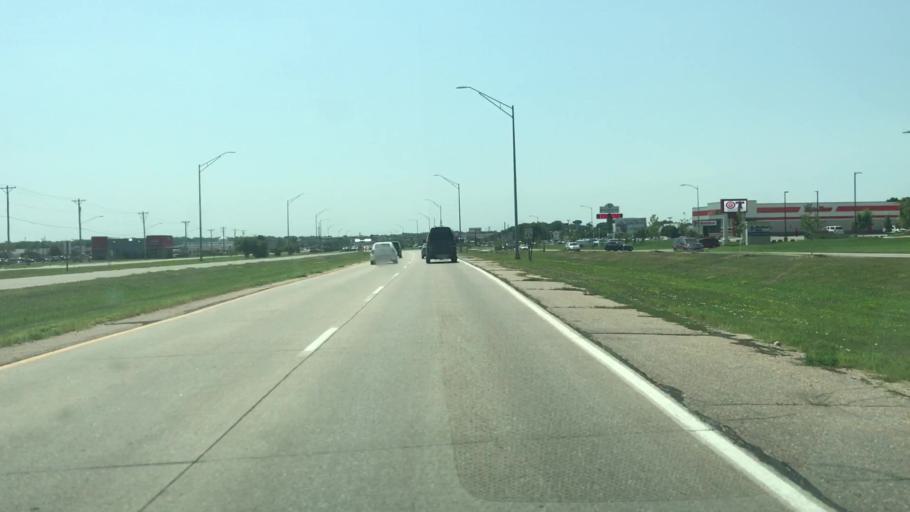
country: US
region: Nebraska
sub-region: Adams County
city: Hastings
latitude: 40.6223
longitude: -98.3829
